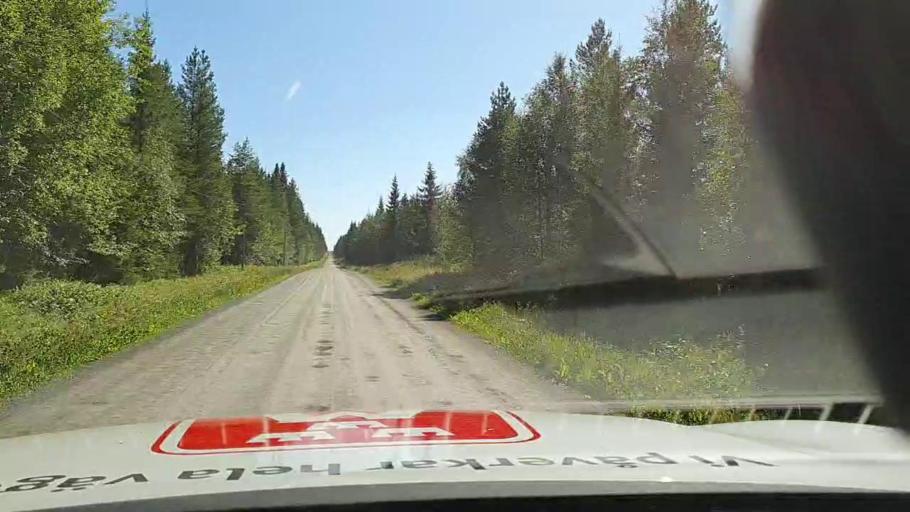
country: SE
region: Jaemtland
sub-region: Krokoms Kommun
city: Krokom
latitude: 63.6957
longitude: 14.6085
